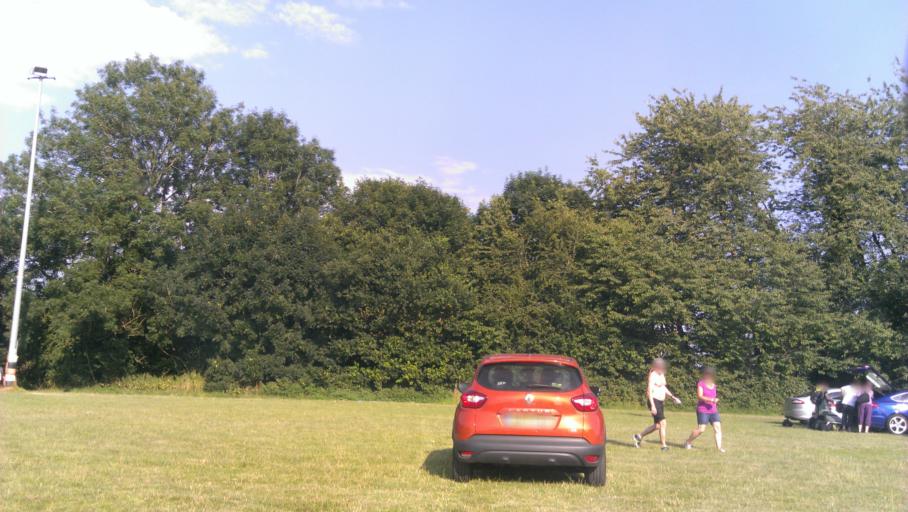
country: GB
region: England
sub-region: Kent
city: Maidstone
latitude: 51.2679
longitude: 0.5377
